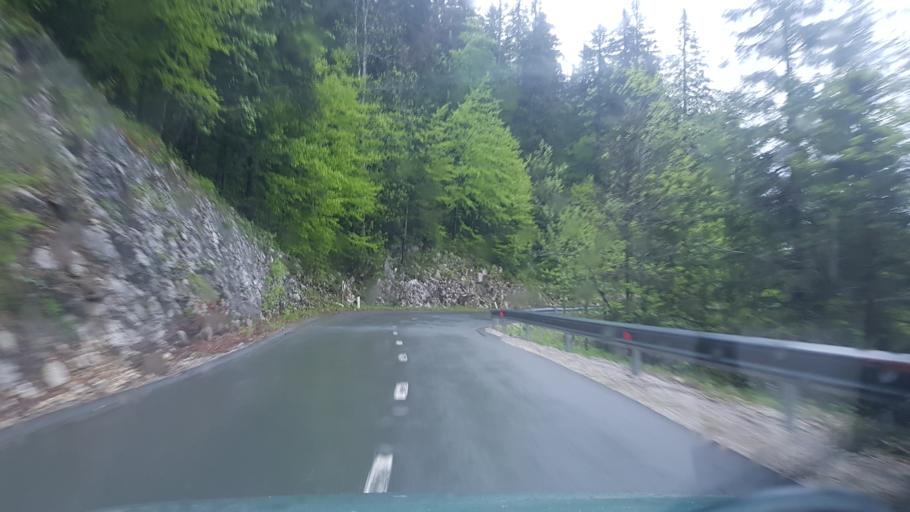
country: SI
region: Bohinj
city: Bohinjska Bistrica
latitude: 46.2477
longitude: 14.0055
